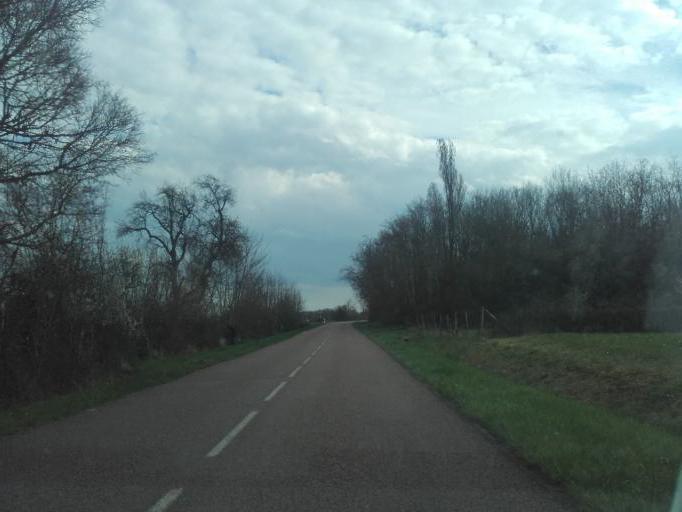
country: FR
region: Bourgogne
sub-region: Departement de la Cote-d'Or
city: Nolay
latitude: 46.9374
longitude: 4.6235
